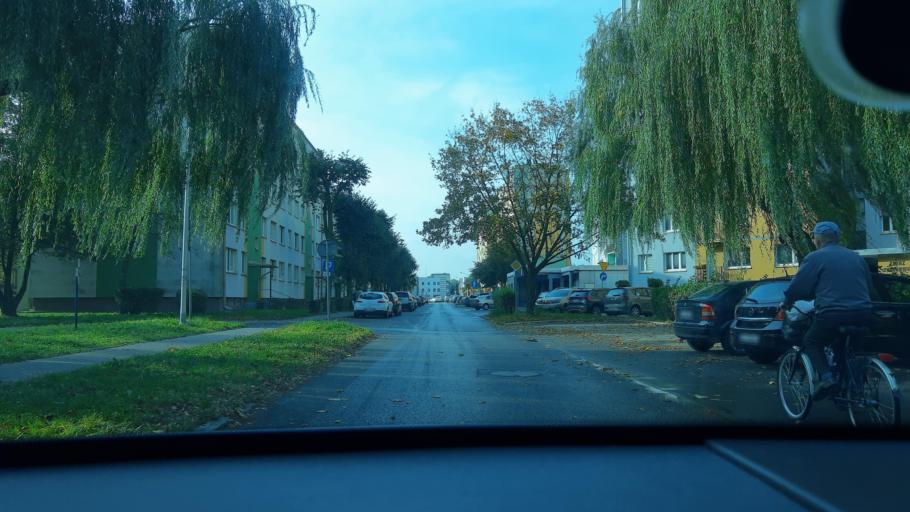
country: PL
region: Lodz Voivodeship
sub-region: Powiat sieradzki
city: Sieradz
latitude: 51.5905
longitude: 18.7221
